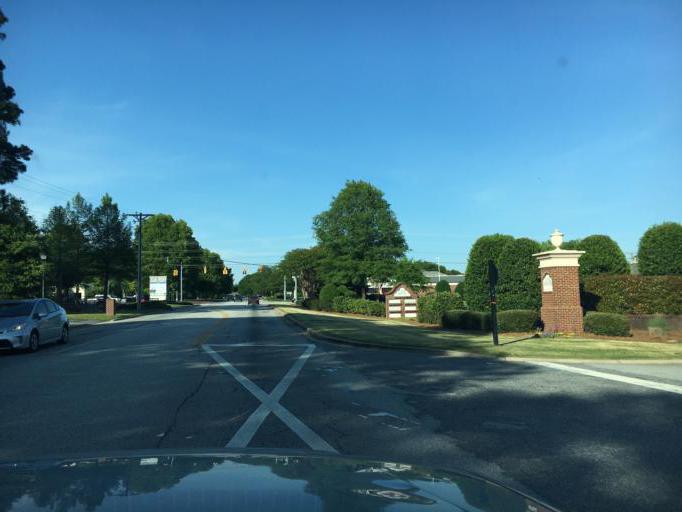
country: US
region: South Carolina
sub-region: Greenville County
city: Five Forks
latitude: 34.8142
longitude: -82.2751
